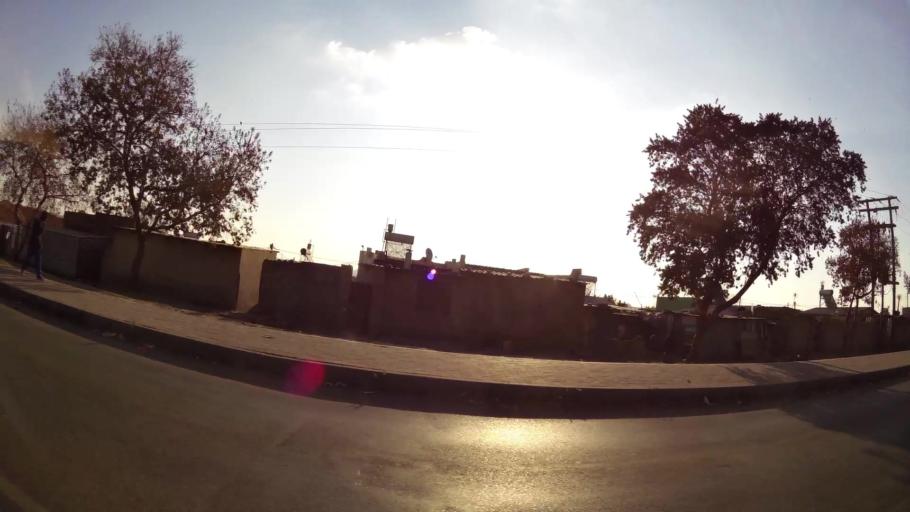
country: ZA
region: Gauteng
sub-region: Ekurhuleni Metropolitan Municipality
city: Tembisa
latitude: -25.9966
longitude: 28.1982
